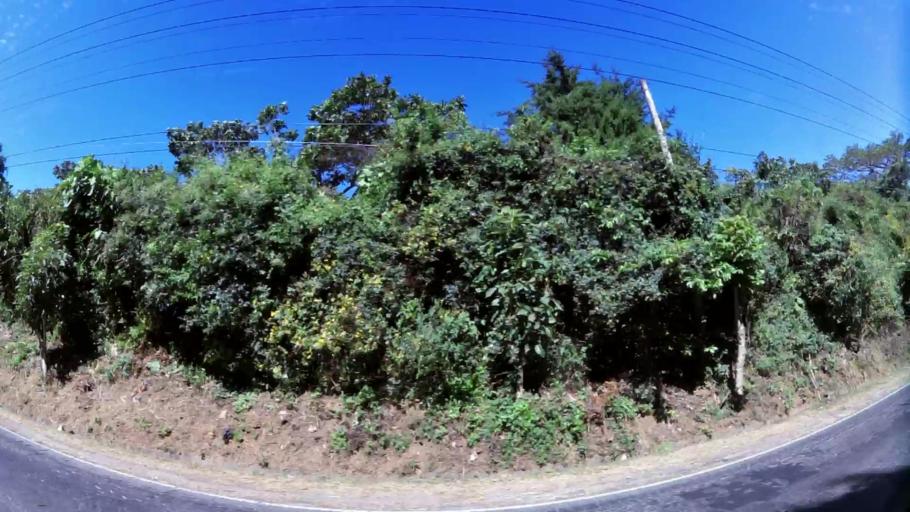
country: SV
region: Ahuachapan
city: Concepcion de Ataco
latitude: 13.8615
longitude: -89.8485
